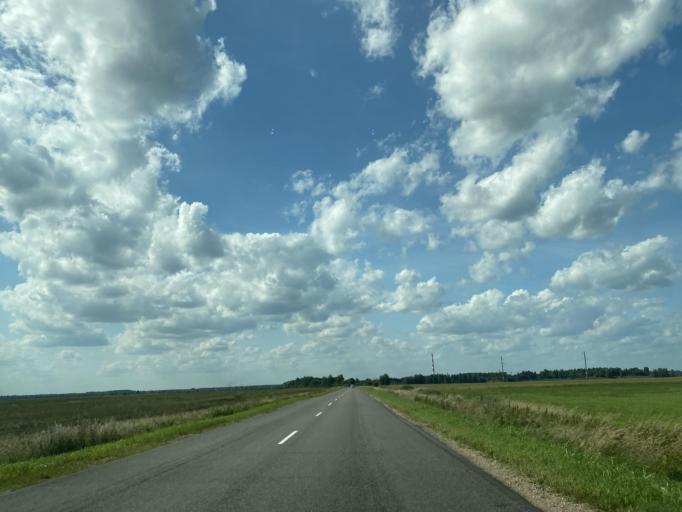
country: BY
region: Minsk
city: Horad Zhodzina
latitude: 54.0759
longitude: 28.3951
